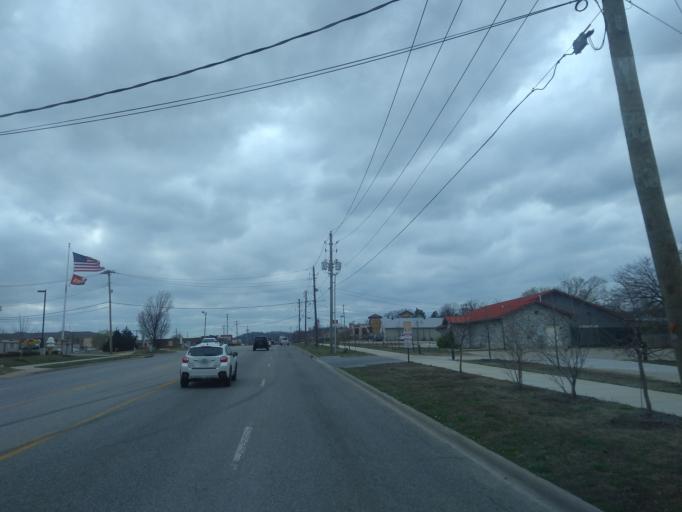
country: US
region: Arkansas
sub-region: Washington County
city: Fayetteville
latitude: 36.0568
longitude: -94.1820
